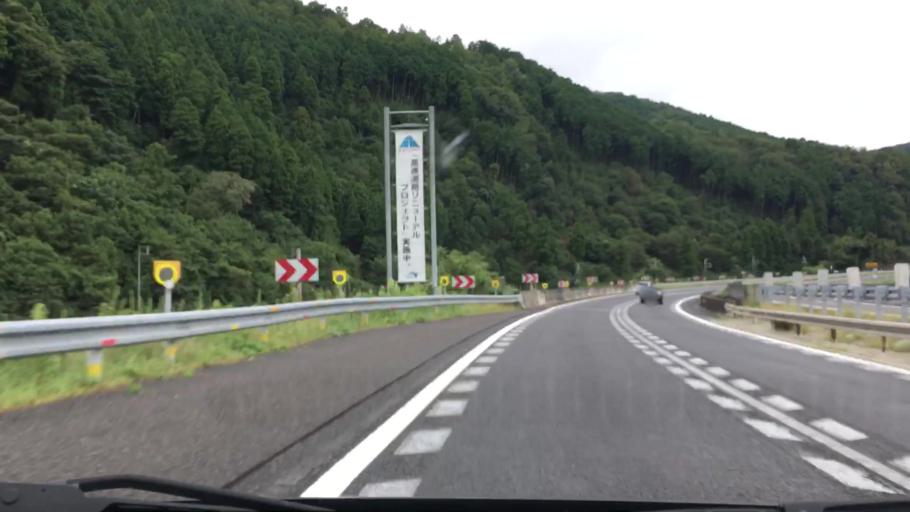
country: JP
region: Hyogo
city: Yamazakicho-nakabirose
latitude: 35.0430
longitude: 134.4493
